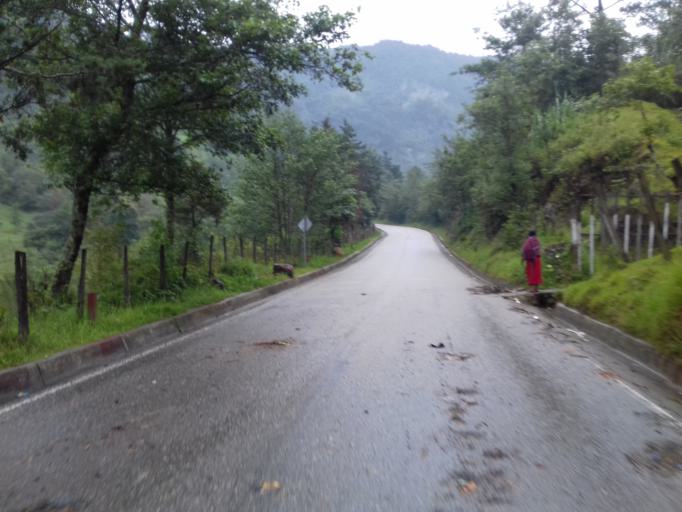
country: GT
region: Quiche
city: Nebaj
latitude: 15.3877
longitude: -91.1177
